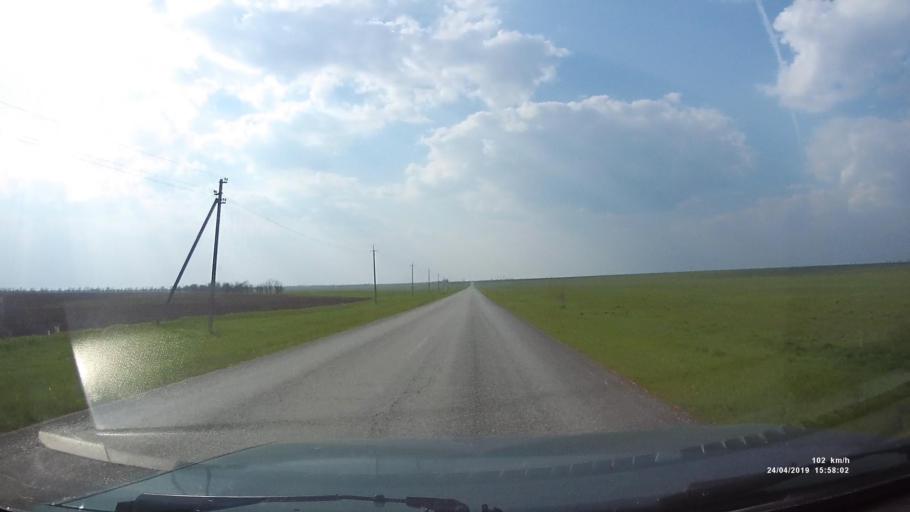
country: RU
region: Kalmykiya
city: Yashalta
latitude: 46.6104
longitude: 42.4976
